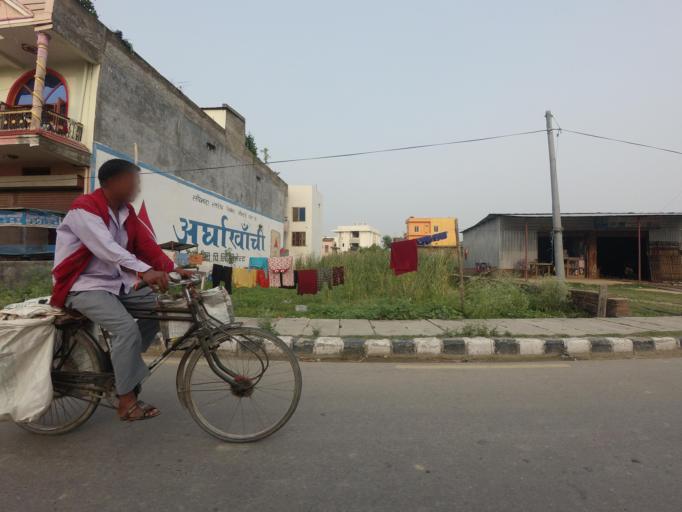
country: NP
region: Western Region
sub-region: Lumbini Zone
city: Bhairahawa
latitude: 27.5116
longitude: 83.4436
